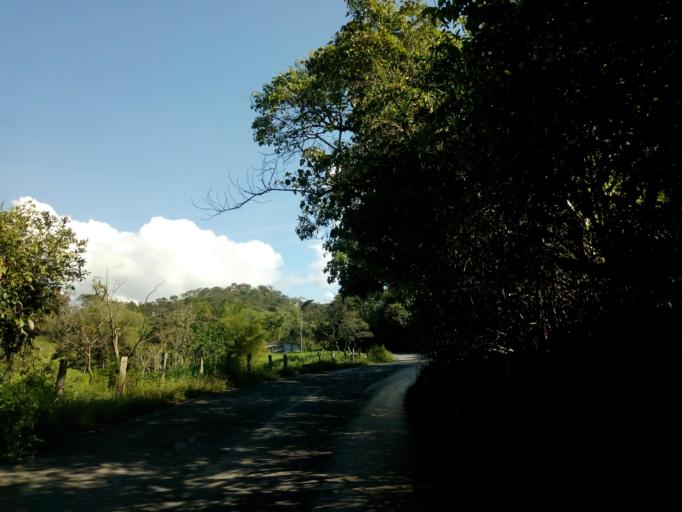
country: CO
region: Boyaca
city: Moniquira
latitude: 5.8667
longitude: -73.5531
